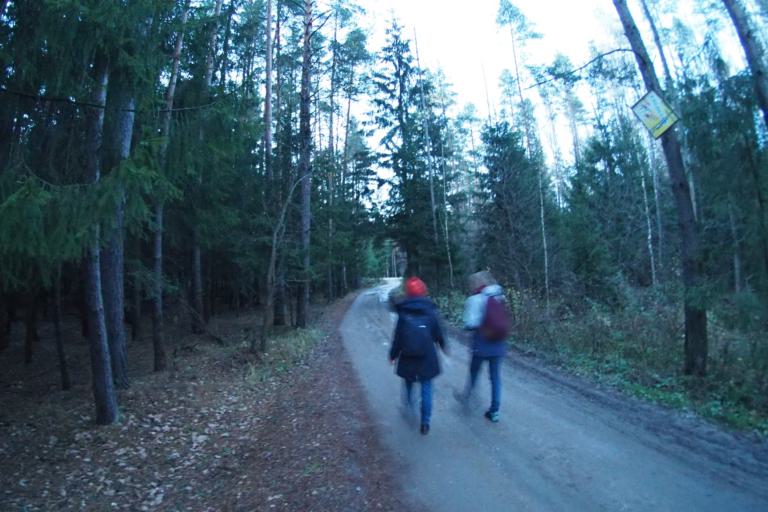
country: RU
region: Moskovskaya
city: Davydovo
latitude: 55.5569
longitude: 38.8368
